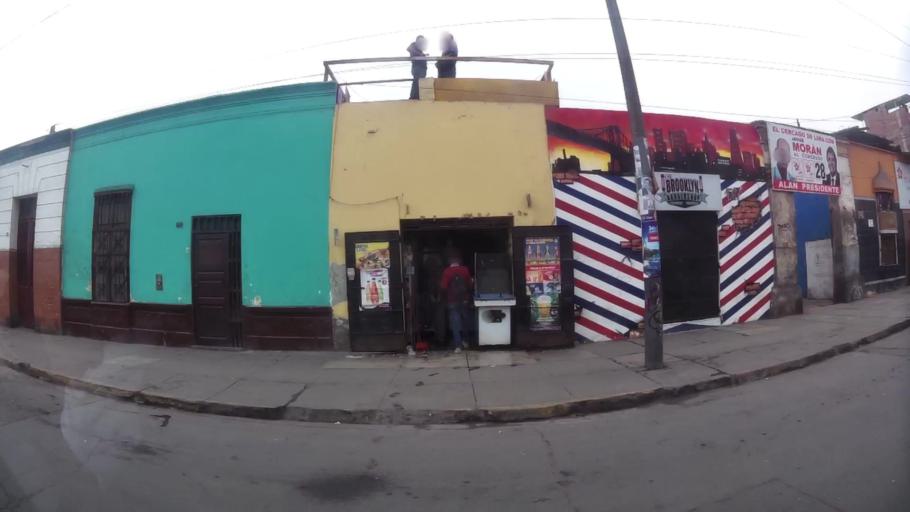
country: PE
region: Lima
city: Lima
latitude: -12.0522
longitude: -77.0138
